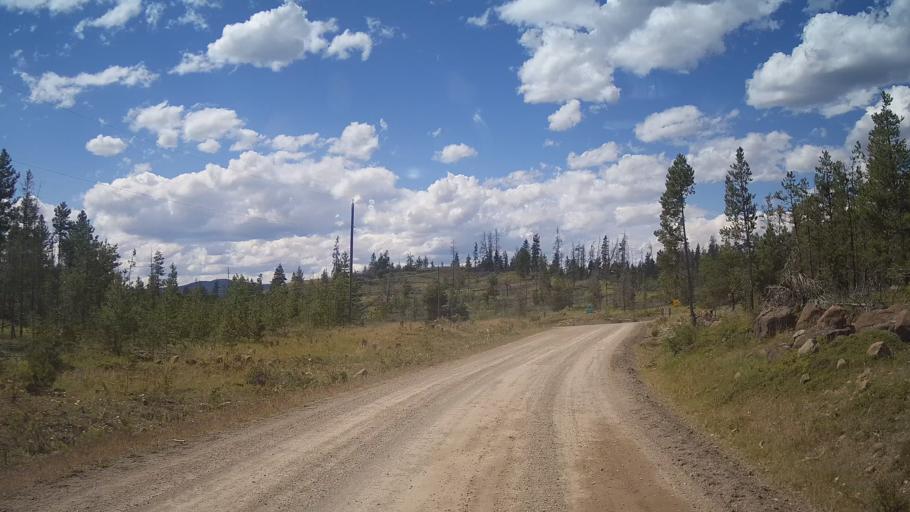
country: CA
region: British Columbia
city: Lillooet
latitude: 51.3355
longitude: -121.9693
